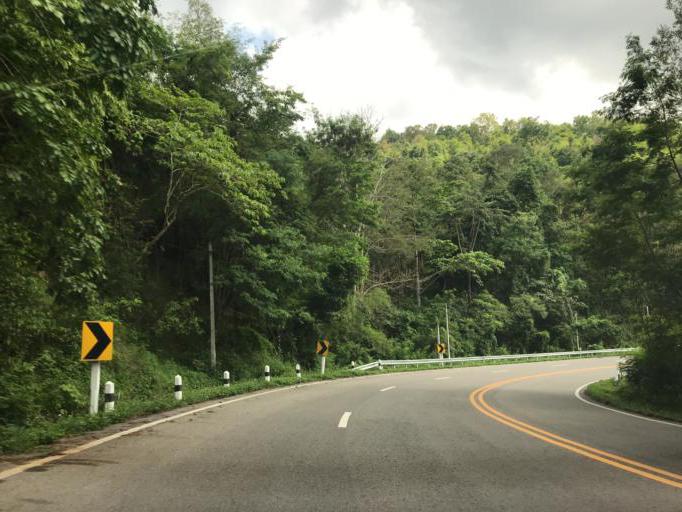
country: TH
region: Phayao
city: Phayao
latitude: 19.0688
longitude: 99.8108
